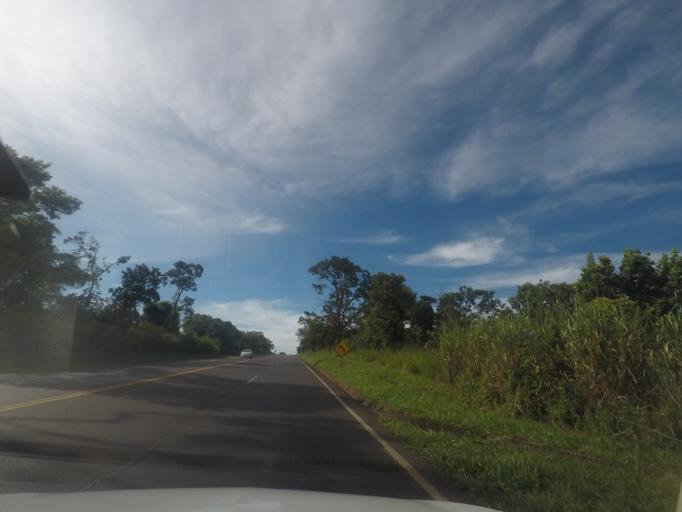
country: BR
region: Minas Gerais
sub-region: Monte Alegre De Minas
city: Monte Alegre de Minas
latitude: -18.9016
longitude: -49.0419
